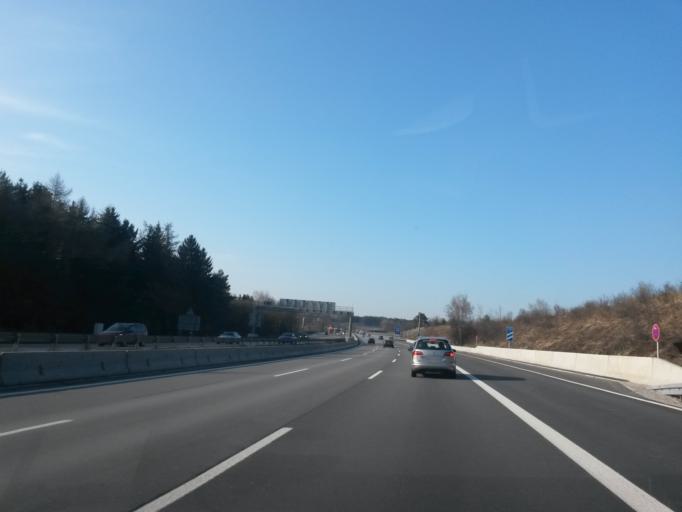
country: DE
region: Bavaria
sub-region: Upper Bavaria
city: Schweitenkirchen
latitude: 48.5478
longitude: 11.5936
